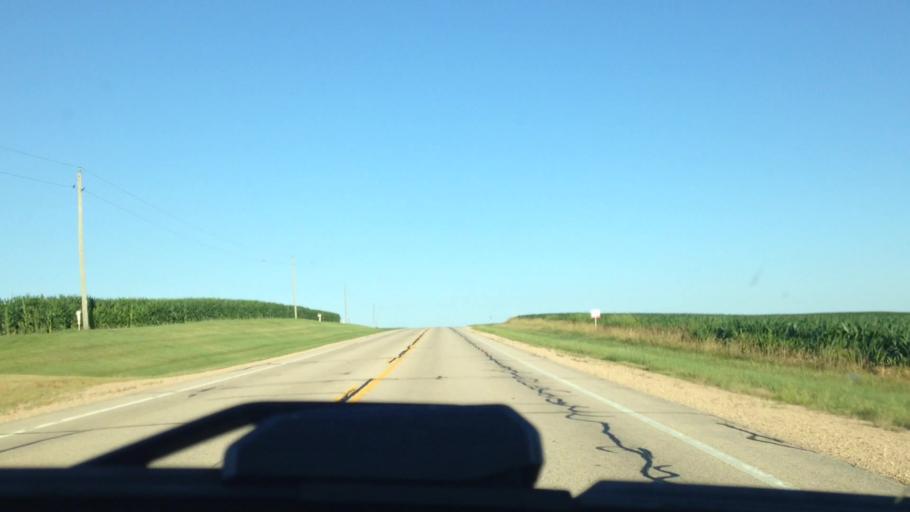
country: US
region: Wisconsin
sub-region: Columbia County
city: Rio
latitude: 43.3407
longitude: -89.2144
